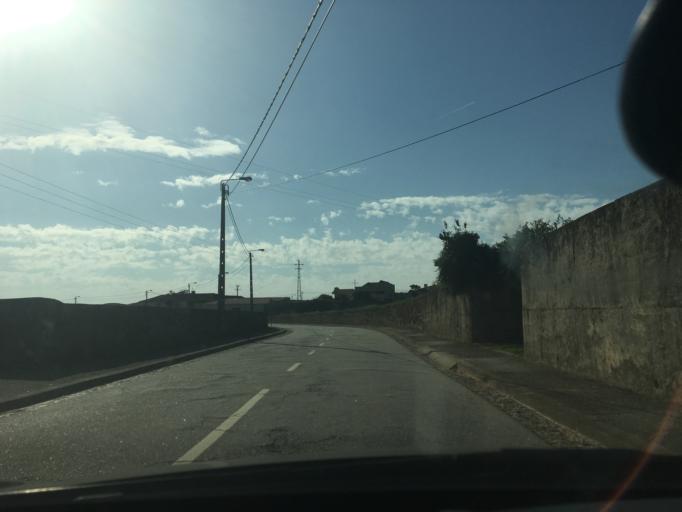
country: PT
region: Porto
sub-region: Maia
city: Gemunde
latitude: 41.2497
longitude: -8.6421
